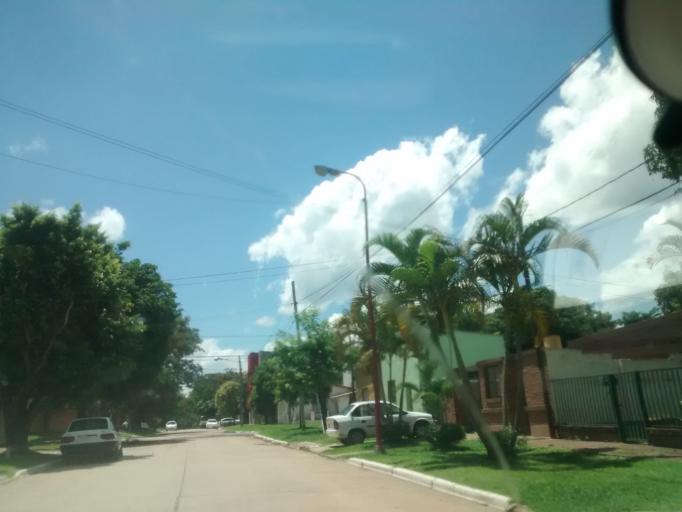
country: AR
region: Chaco
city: Resistencia
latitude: -27.4372
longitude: -58.9861
